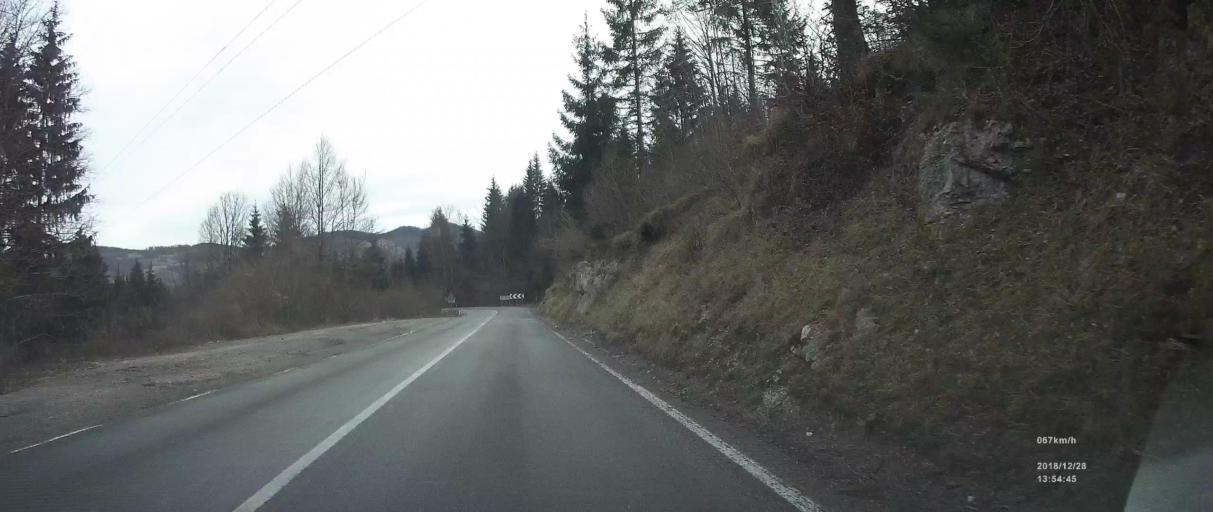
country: HR
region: Primorsko-Goranska
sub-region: Grad Delnice
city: Delnice
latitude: 45.3842
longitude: 14.8672
